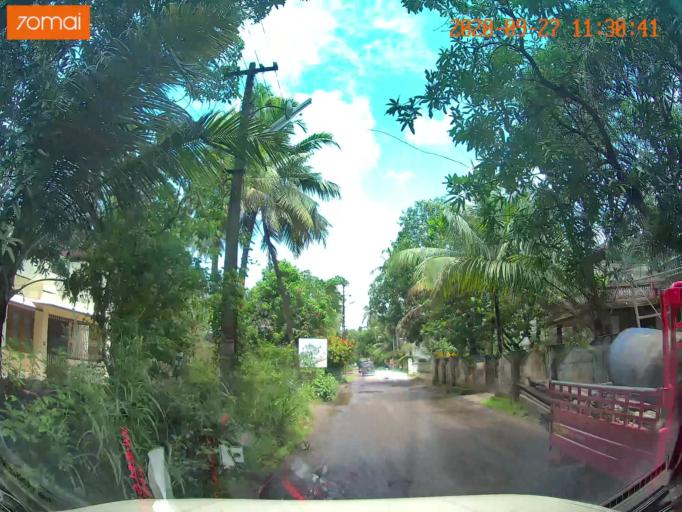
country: IN
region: Kerala
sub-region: Thrissur District
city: Thanniyam
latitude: 10.4199
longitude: 76.1339
